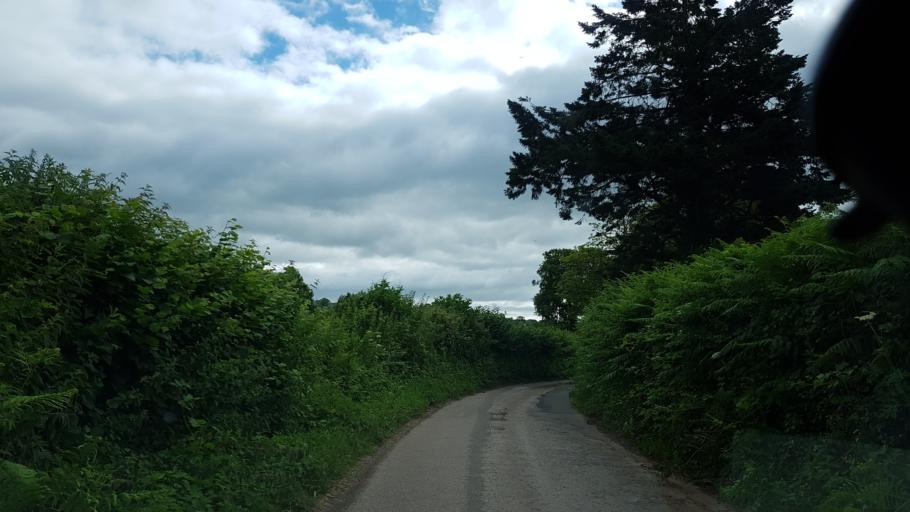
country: GB
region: Wales
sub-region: Monmouthshire
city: Abergavenny
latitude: 51.7959
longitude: -3.0040
